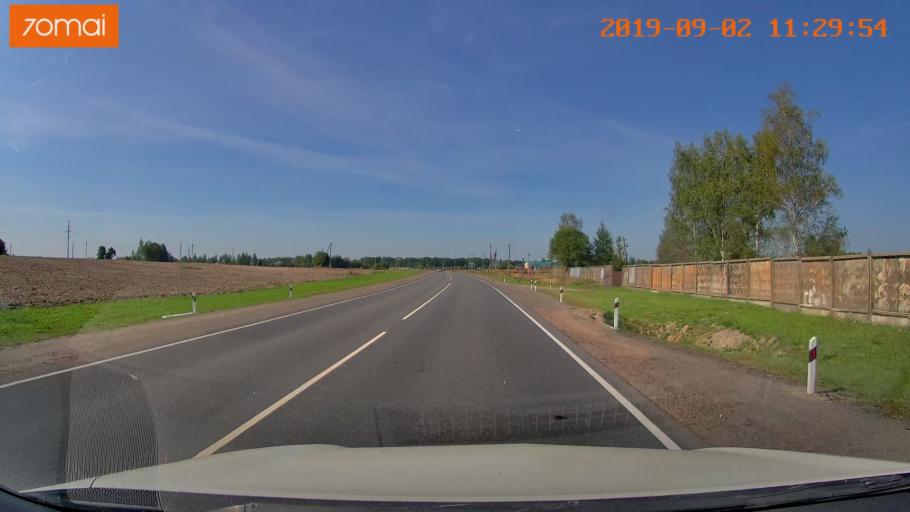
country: RU
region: Smolensk
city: Roslavl'
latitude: 53.9880
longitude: 32.8477
